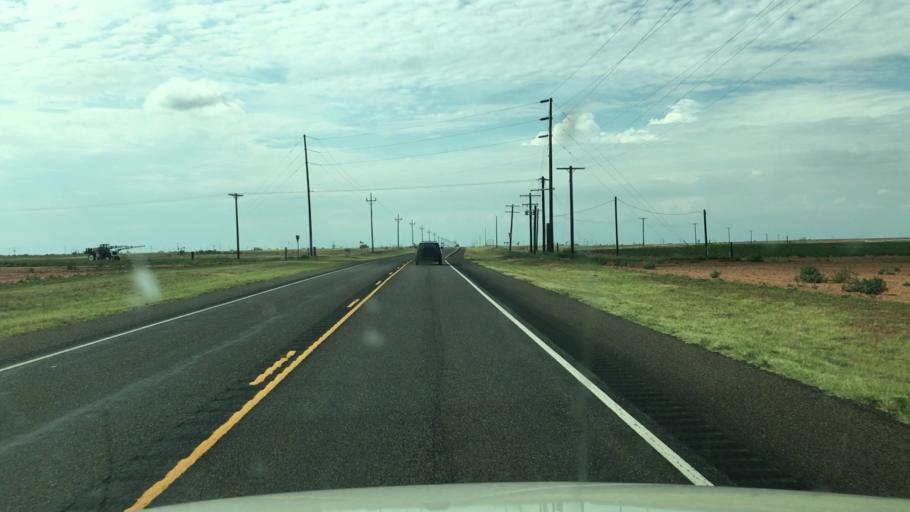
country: US
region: Texas
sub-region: Dawson County
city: Lamesa
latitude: 32.8889
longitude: -102.0886
